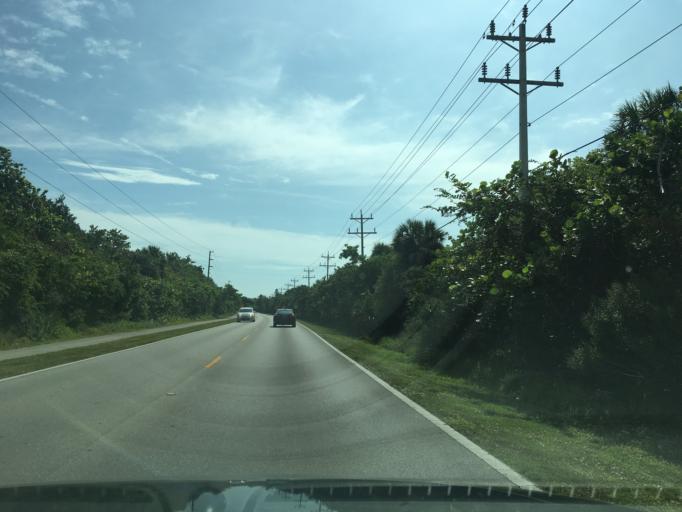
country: US
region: Florida
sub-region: Lee County
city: Saint James City
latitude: 26.4600
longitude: -82.1461
